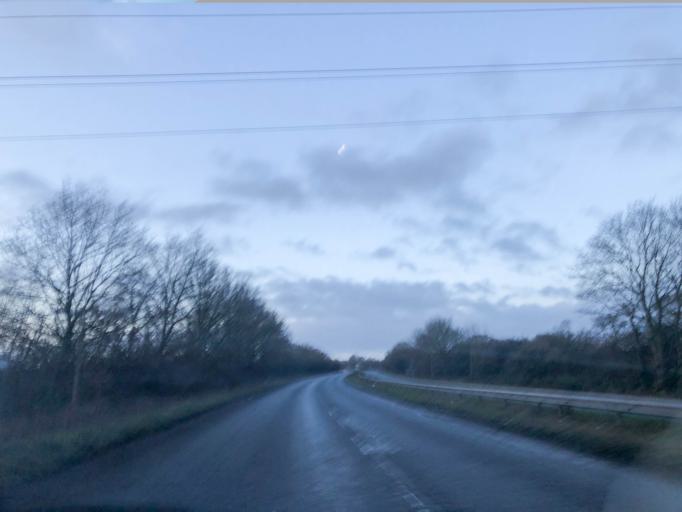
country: GB
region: England
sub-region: Solihull
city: Tidbury Green
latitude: 52.4026
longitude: -1.8882
